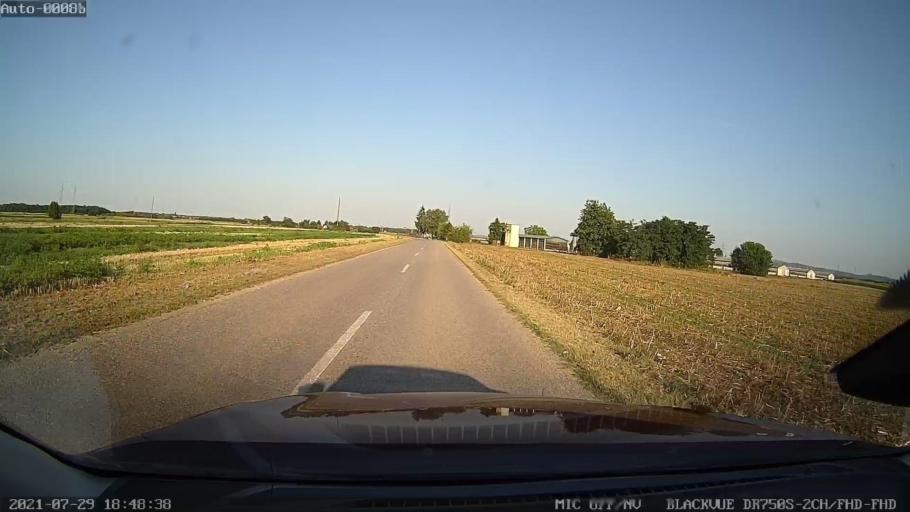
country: HR
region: Varazdinska
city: Sracinec
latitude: 46.3112
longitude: 16.2932
